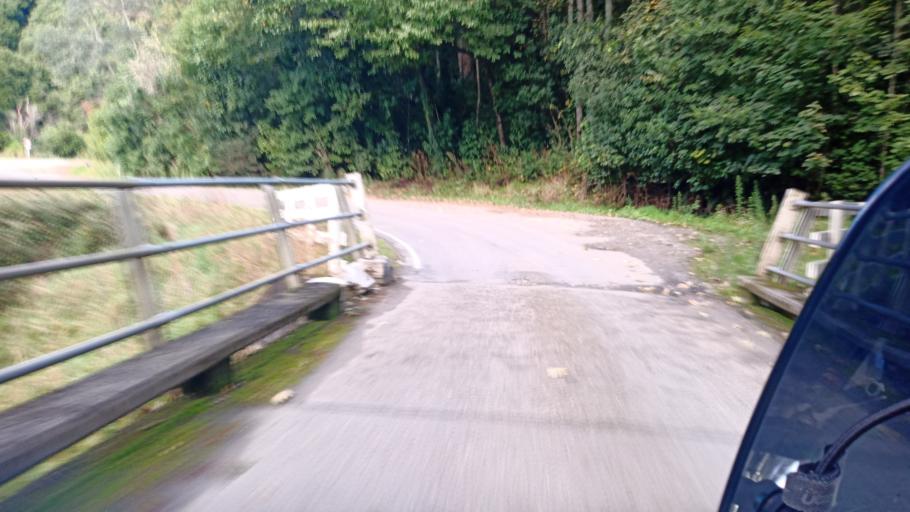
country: NZ
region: Gisborne
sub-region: Gisborne District
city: Gisborne
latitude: -38.5330
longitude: 177.5335
